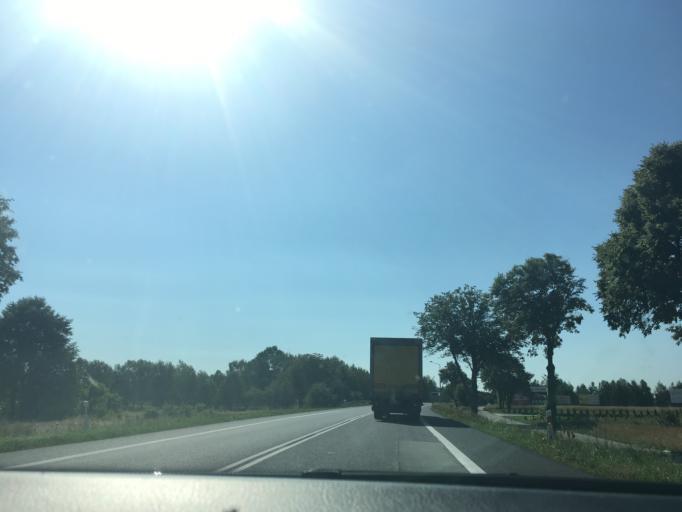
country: PL
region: Lublin Voivodeship
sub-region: Powiat lubartowski
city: Lubartow
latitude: 51.4840
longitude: 22.5862
